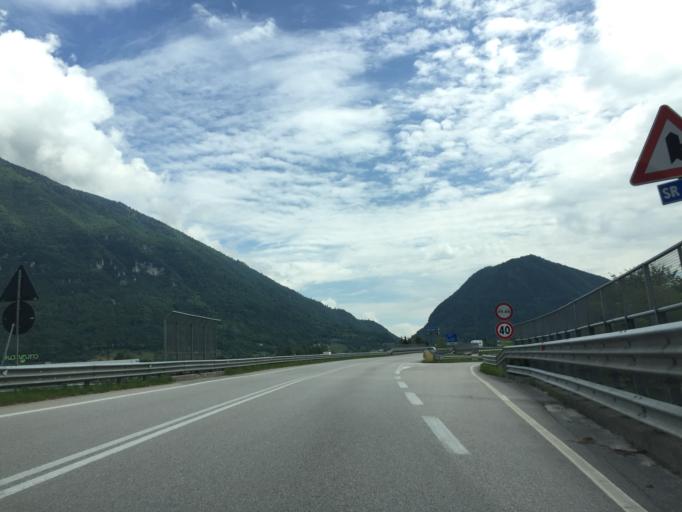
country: IT
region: Veneto
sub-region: Provincia di Belluno
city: Fonzaso
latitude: 46.0008
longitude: 11.8054
